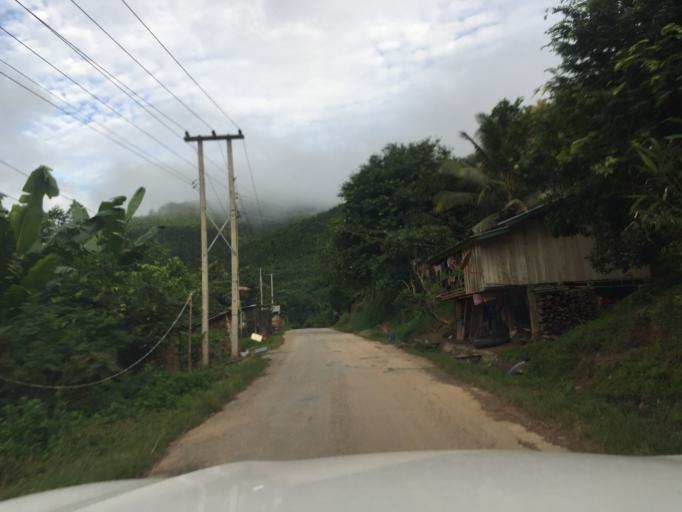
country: LA
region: Phongsali
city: Khoa
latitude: 21.1032
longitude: 102.2882
